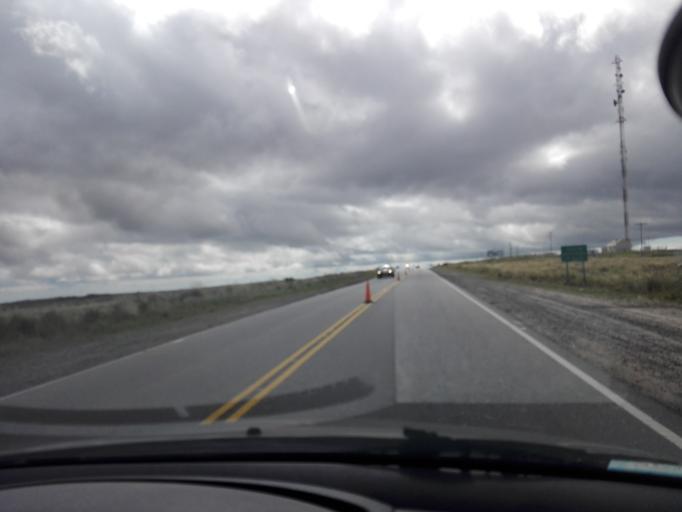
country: AR
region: Cordoba
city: Mina Clavero
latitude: -31.6178
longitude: -64.8690
